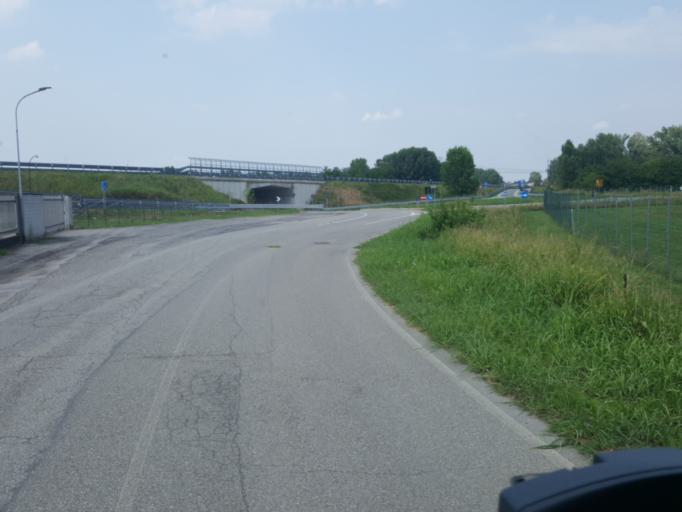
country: IT
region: Lombardy
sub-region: Provincia di Lodi
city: Guardamiglio
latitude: 45.1120
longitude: 9.6883
